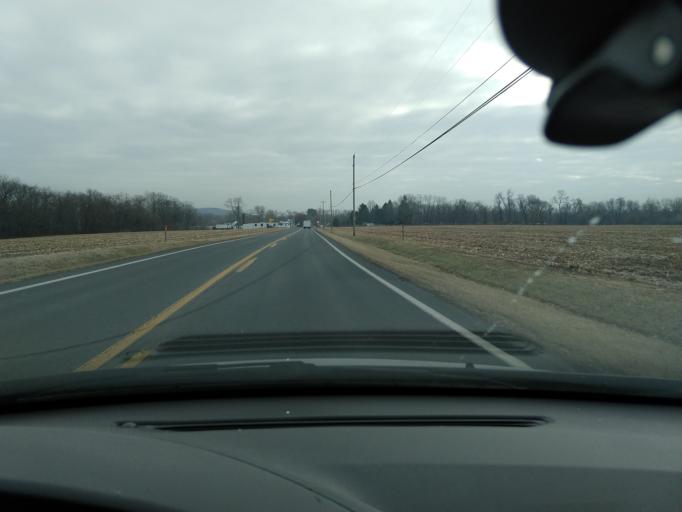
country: US
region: Pennsylvania
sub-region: Berks County
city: Amity Gardens
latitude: 40.2576
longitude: -75.7441
